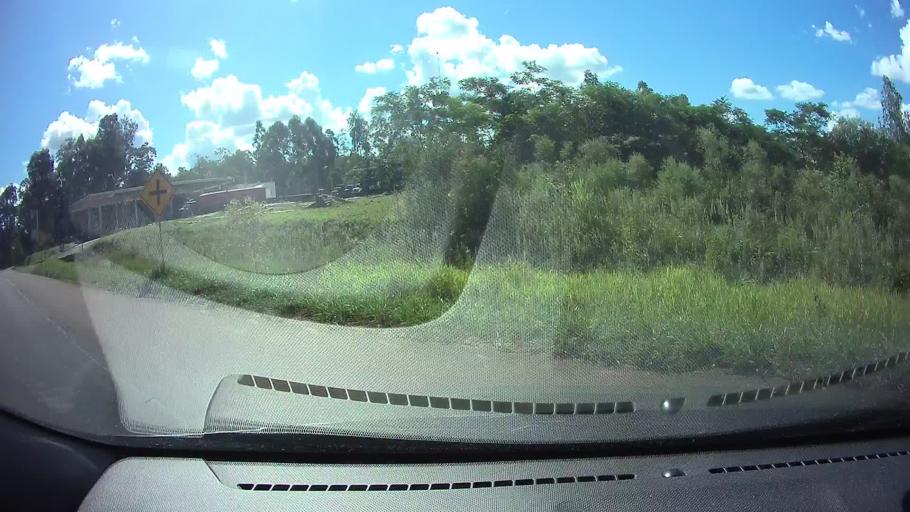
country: PY
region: Guaira
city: Coronel Martinez
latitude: -25.7660
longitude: -56.6525
